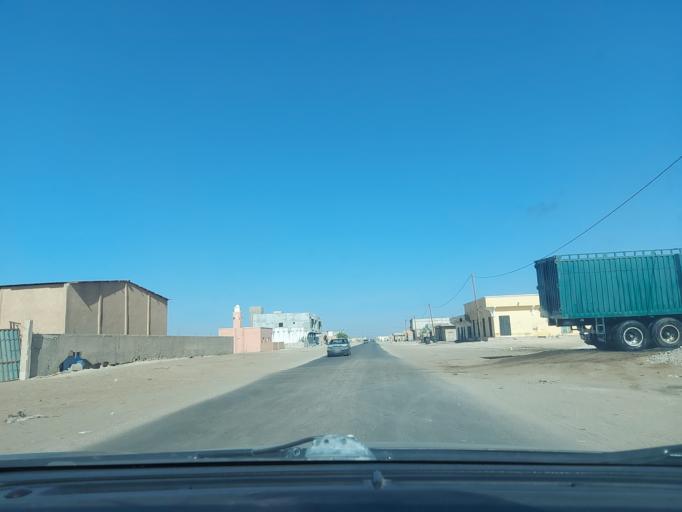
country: MR
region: Nouakchott
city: Nouakchott
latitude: 18.0104
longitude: -15.9785
